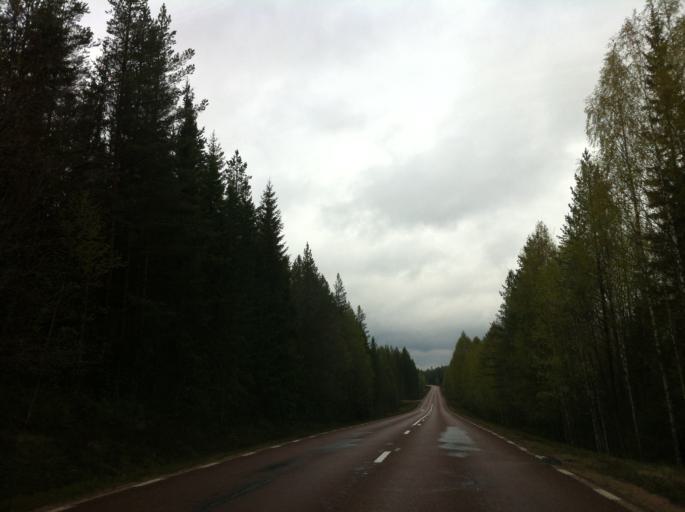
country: SE
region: Jaemtland
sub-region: Harjedalens Kommun
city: Sveg
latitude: 61.8796
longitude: 14.6282
